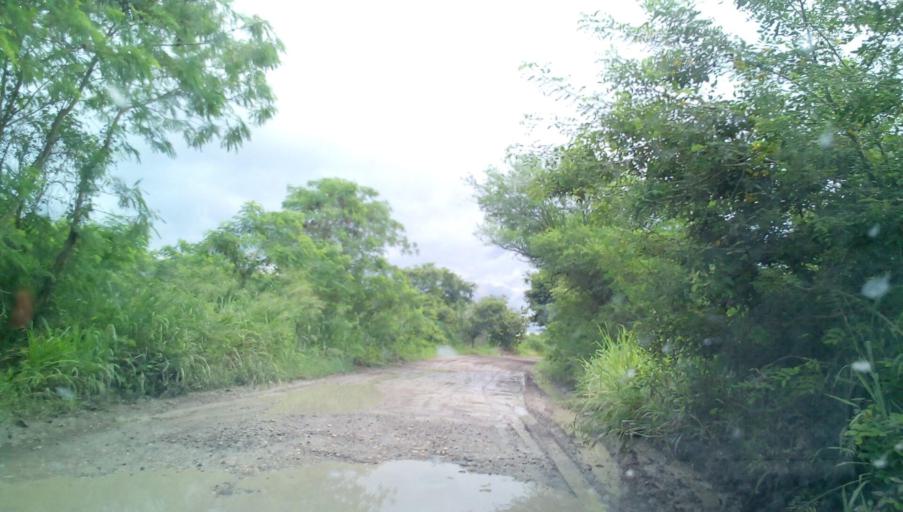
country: MX
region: Veracruz
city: Panuco
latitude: 21.8440
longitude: -98.1340
